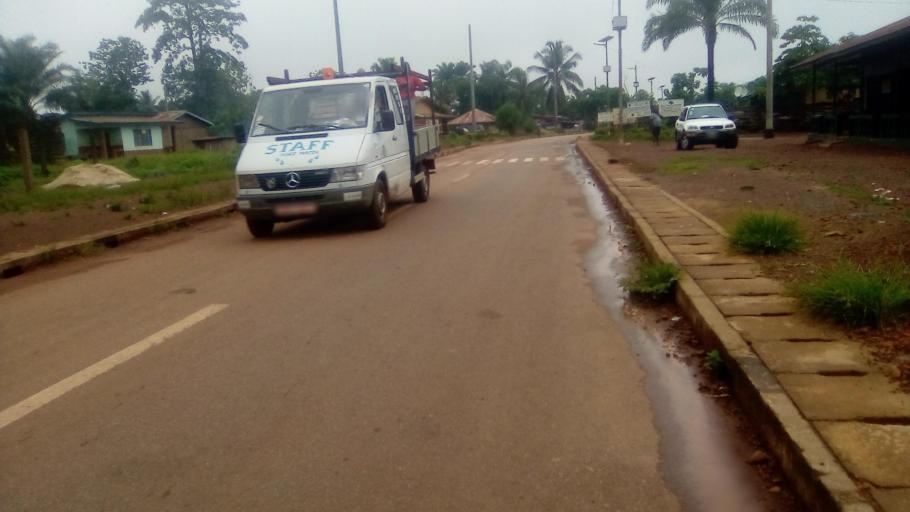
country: SL
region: Southern Province
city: Moyamba
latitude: 8.1509
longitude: -12.4330
